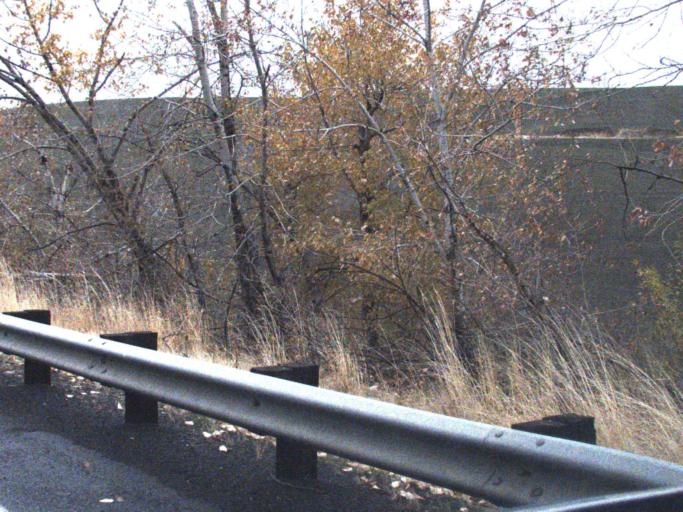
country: US
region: Washington
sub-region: Walla Walla County
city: Waitsburg
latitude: 46.1484
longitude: -118.1418
